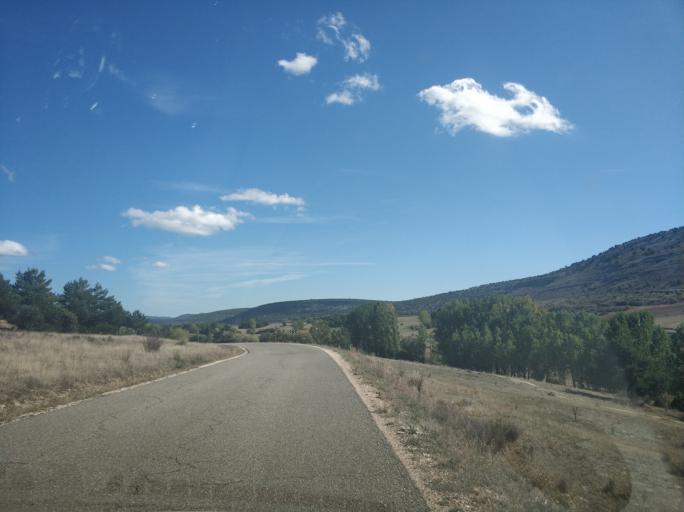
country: ES
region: Castille and Leon
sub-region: Provincia de Burgos
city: Rabanera del Pinar
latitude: 41.8541
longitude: -3.2179
